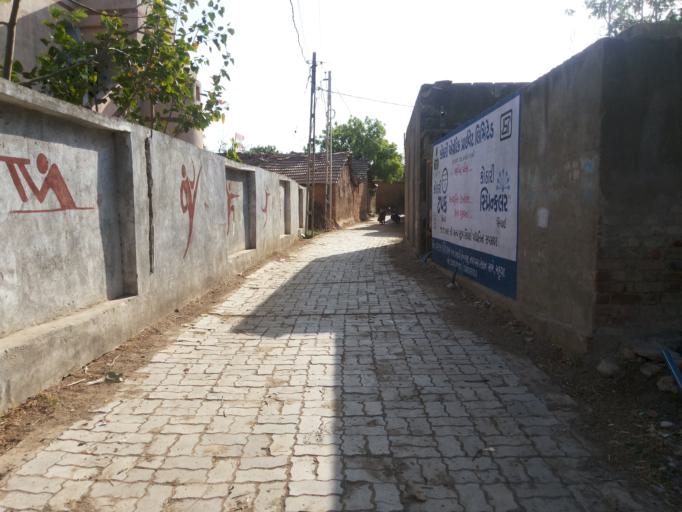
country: IN
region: Gujarat
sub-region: Bhavnagar
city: Katpur
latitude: 21.1068
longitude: 71.8342
